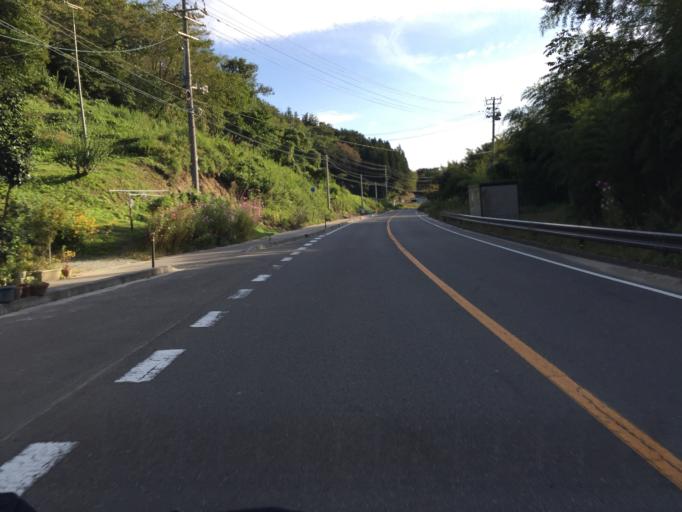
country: JP
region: Fukushima
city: Hobaramachi
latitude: 37.6848
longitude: 140.6185
